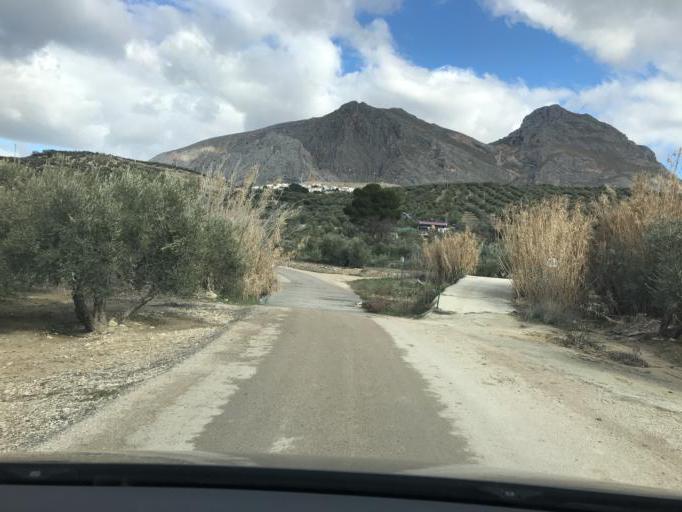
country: ES
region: Andalusia
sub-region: Provincia de Jaen
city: Jimena
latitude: 37.8117
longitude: -3.4260
